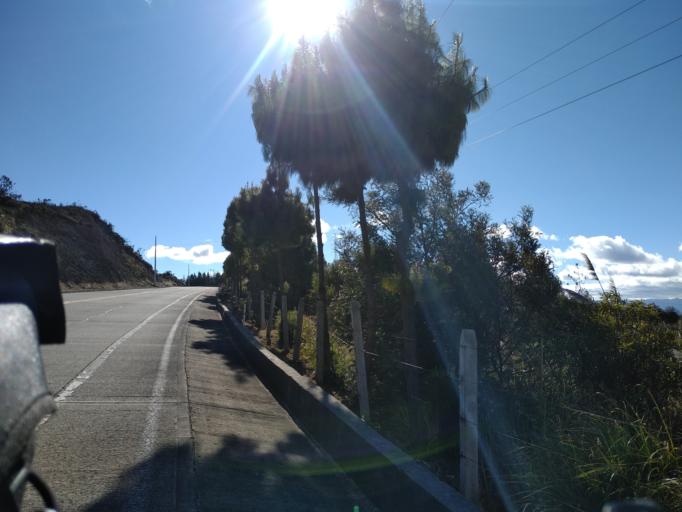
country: EC
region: Azuay
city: Cuenca
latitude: -3.3077
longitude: -79.1278
